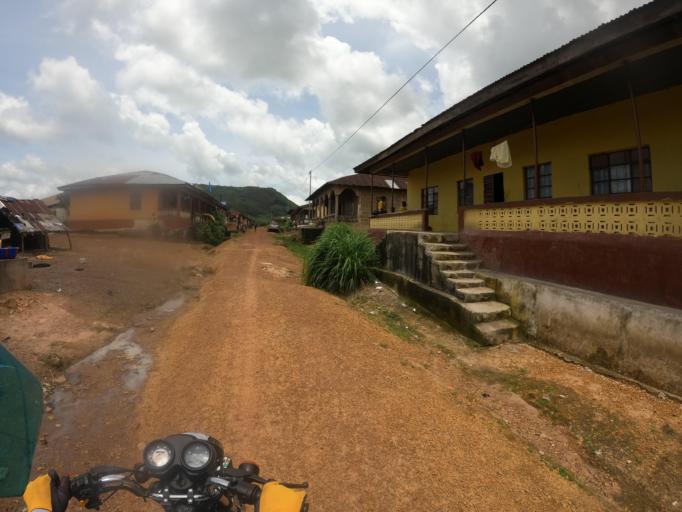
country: SL
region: Northern Province
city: Makeni
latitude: 8.8914
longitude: -12.0505
